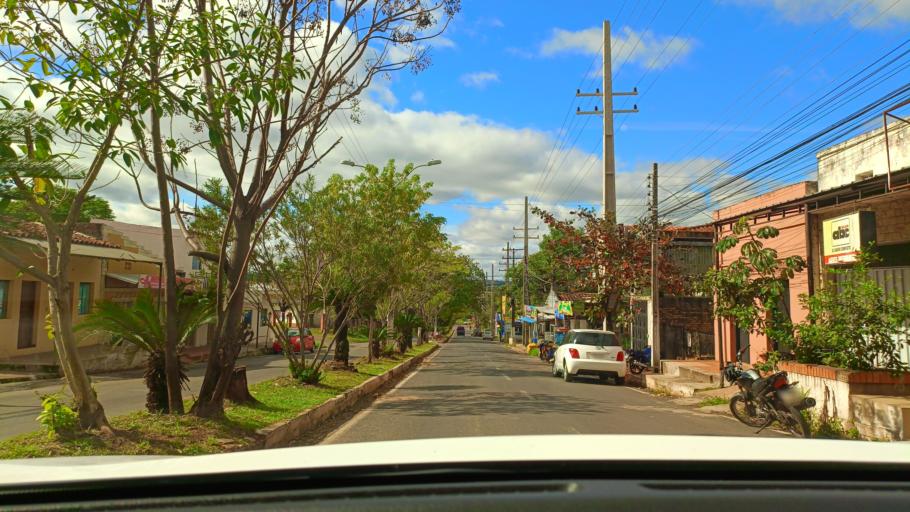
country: PY
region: San Pedro
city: Guayaybi
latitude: -24.6651
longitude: -56.4380
